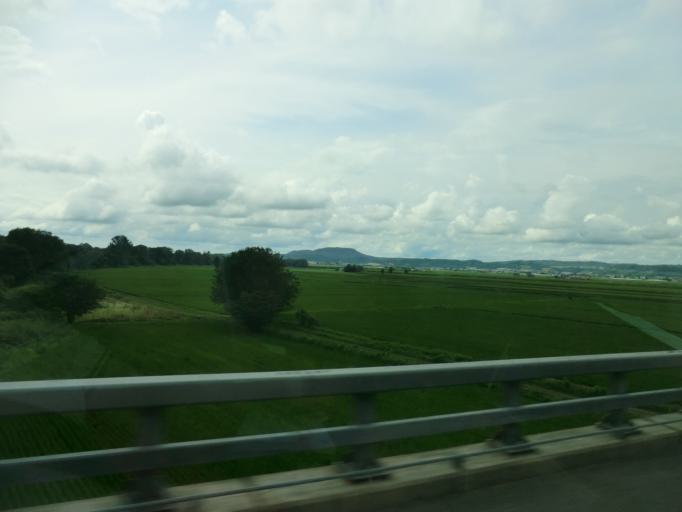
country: JP
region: Hokkaido
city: Fukagawa
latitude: 43.7194
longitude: 142.1653
